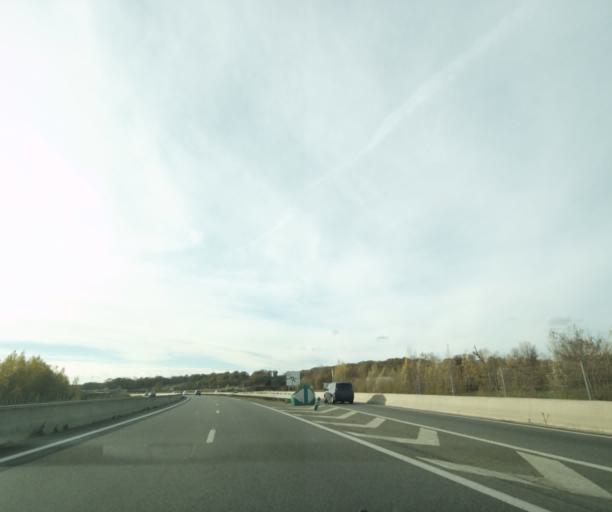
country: FR
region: Midi-Pyrenees
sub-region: Departement de la Haute-Garonne
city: Pibrac
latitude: 43.6050
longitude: 1.2860
